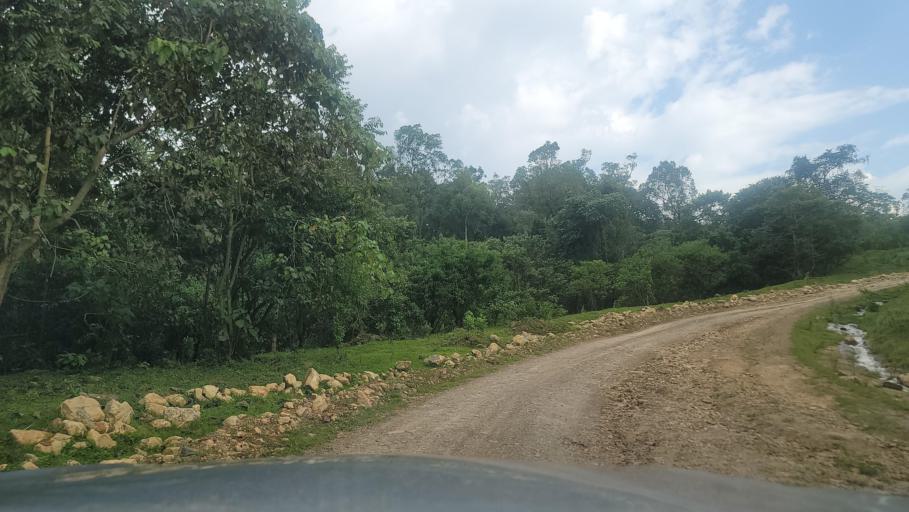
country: ET
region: Southern Nations, Nationalities, and People's Region
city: Bonga
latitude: 7.6028
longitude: 36.2020
